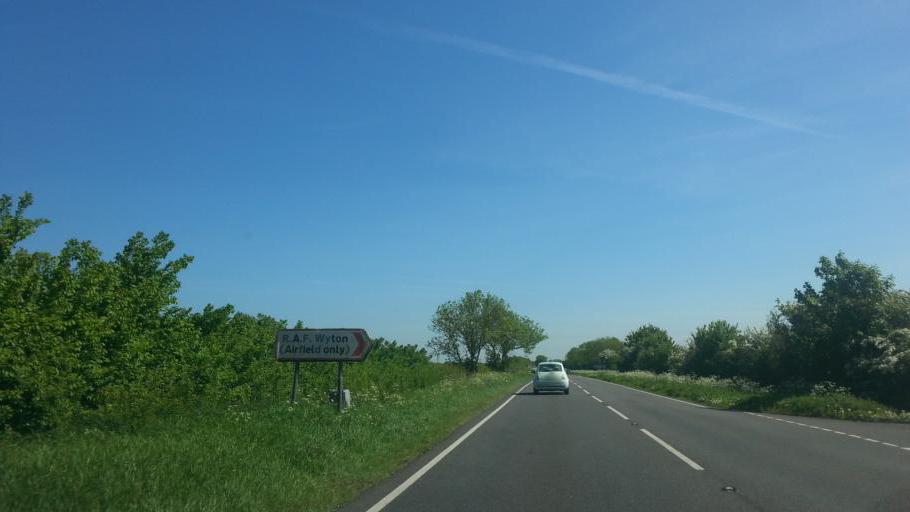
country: GB
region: England
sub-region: Cambridgeshire
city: Hemingford Grey
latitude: 52.3650
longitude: -0.1137
